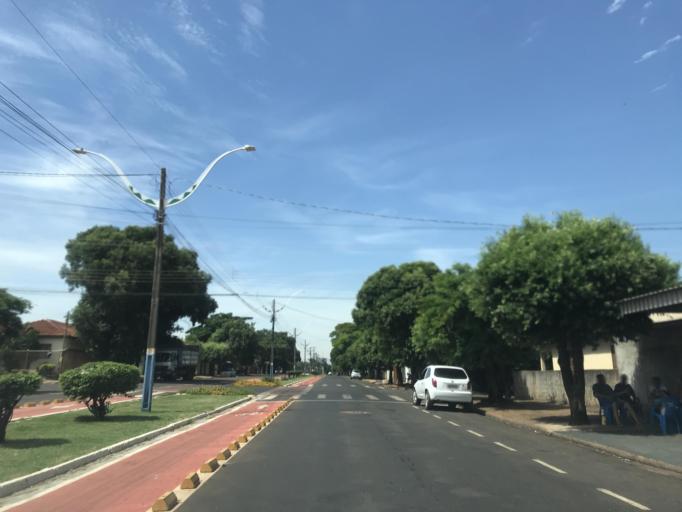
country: BR
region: Parana
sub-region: Terra Rica
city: Terra Rica
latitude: -22.7311
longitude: -52.6246
